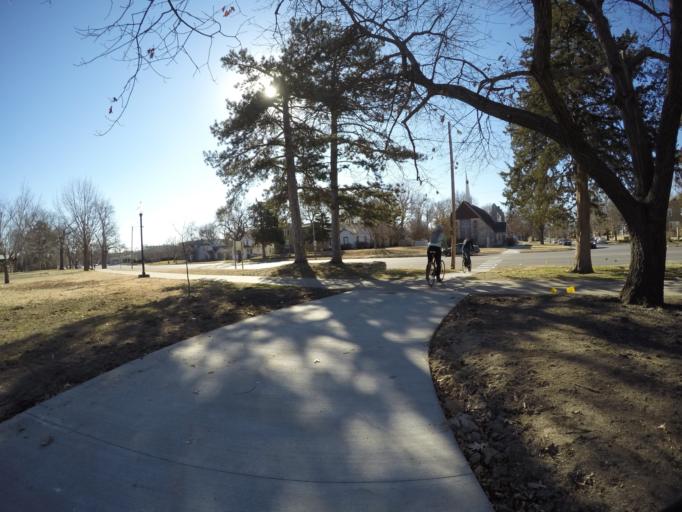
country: US
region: Kansas
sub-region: Riley County
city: Manhattan
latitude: 39.1797
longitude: -96.5765
